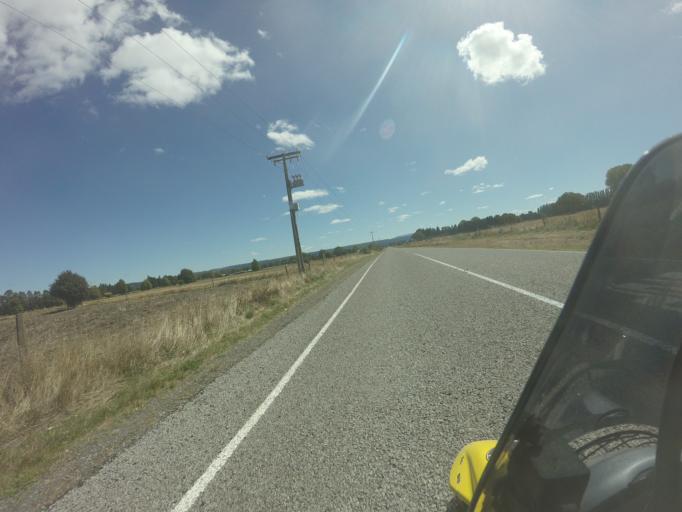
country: NZ
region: Bay of Plenty
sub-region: Whakatane District
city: Murupara
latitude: -38.4668
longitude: 176.7559
